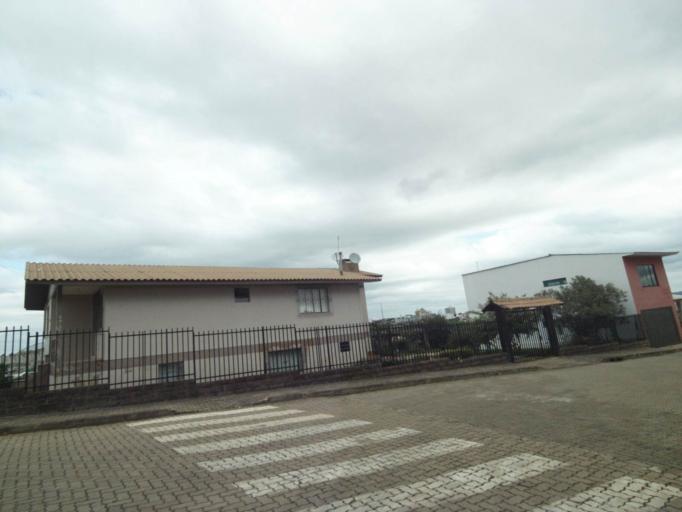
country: BR
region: Rio Grande do Sul
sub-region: Lagoa Vermelha
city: Lagoa Vermelha
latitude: -28.2002
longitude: -51.5272
